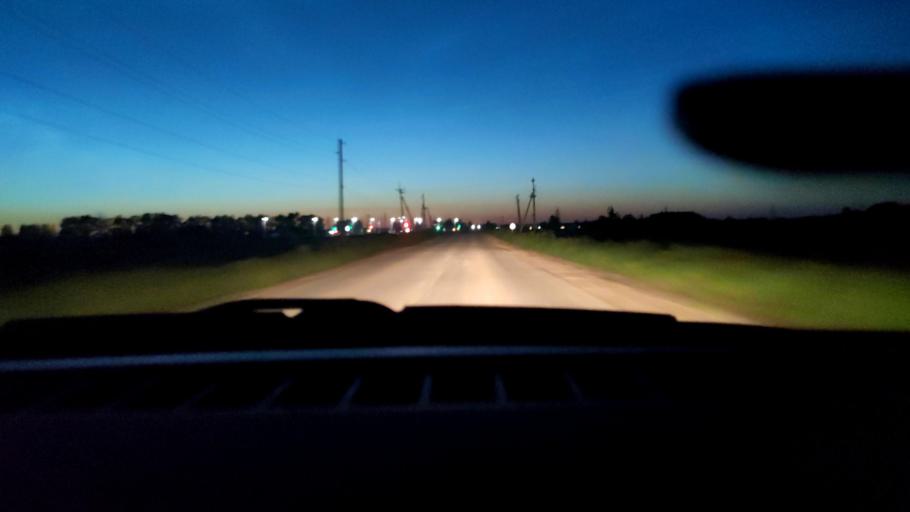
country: RU
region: Perm
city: Kultayevo
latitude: 57.8809
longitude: 55.9222
